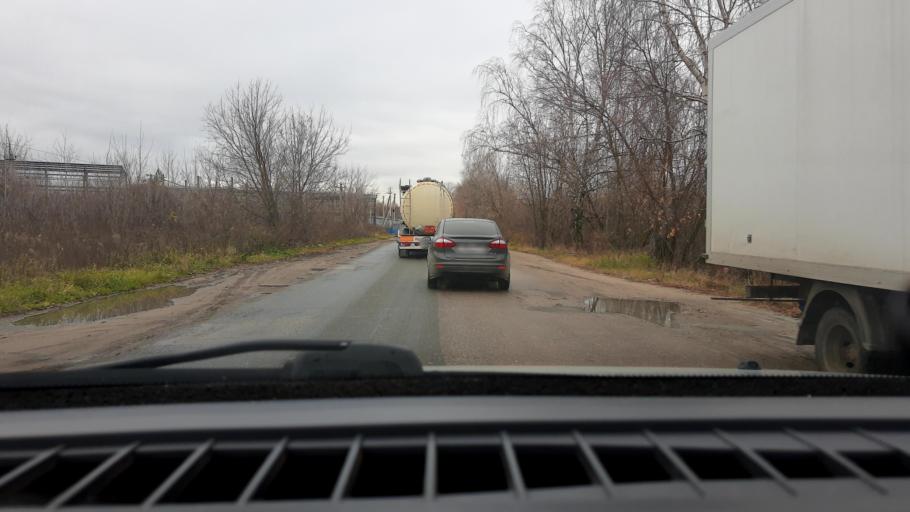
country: RU
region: Nizjnij Novgorod
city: Kstovo
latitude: 56.1930
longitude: 44.1345
